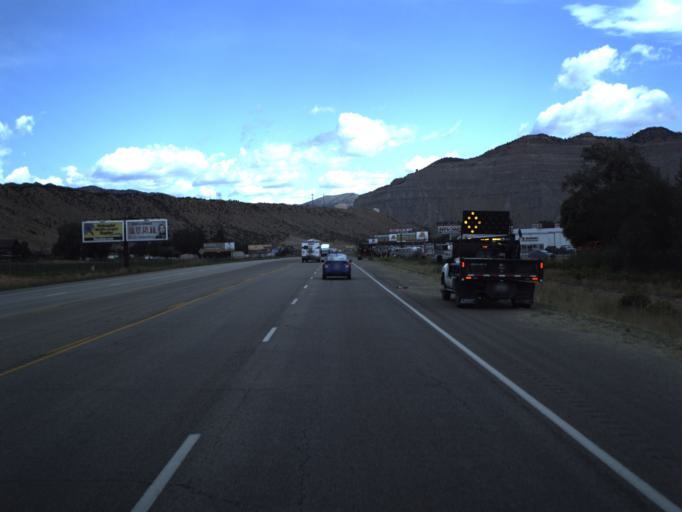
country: US
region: Utah
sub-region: Carbon County
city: Spring Glen
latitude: 39.6651
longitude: -110.8610
